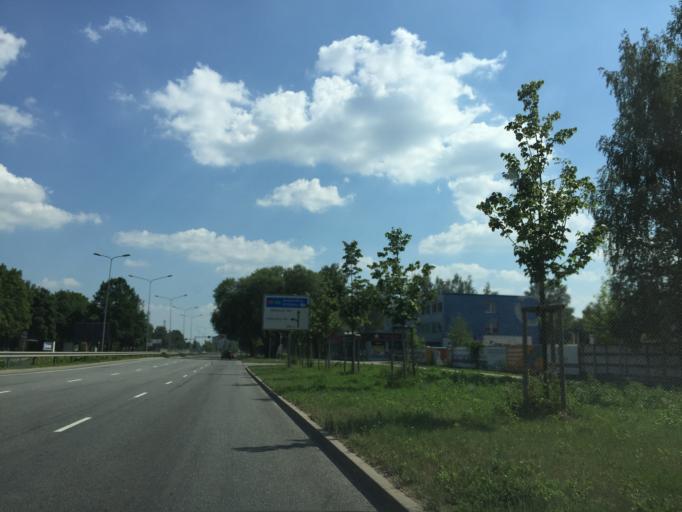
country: LV
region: Riga
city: Riga
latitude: 56.9277
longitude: 24.1858
